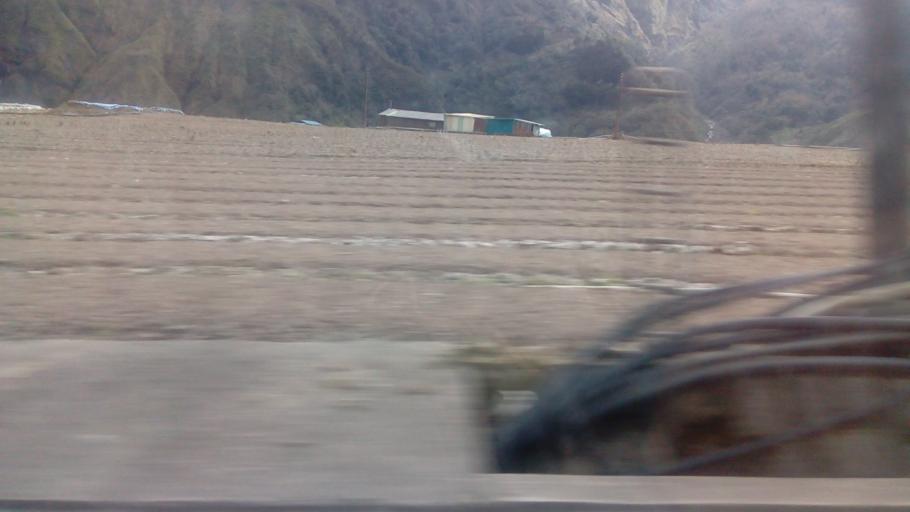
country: TW
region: Taiwan
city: Daxi
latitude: 24.4660
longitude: 121.4016
